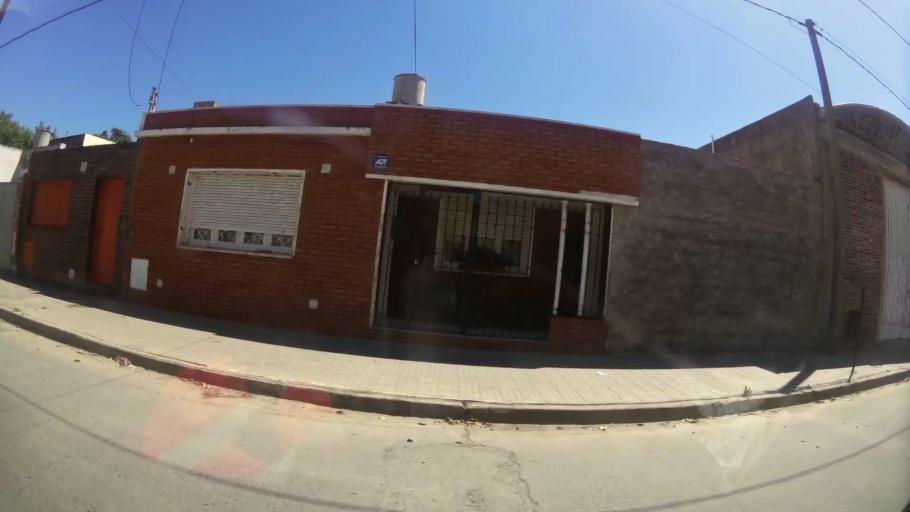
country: AR
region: Cordoba
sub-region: Departamento de Capital
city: Cordoba
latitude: -31.4256
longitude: -64.2020
